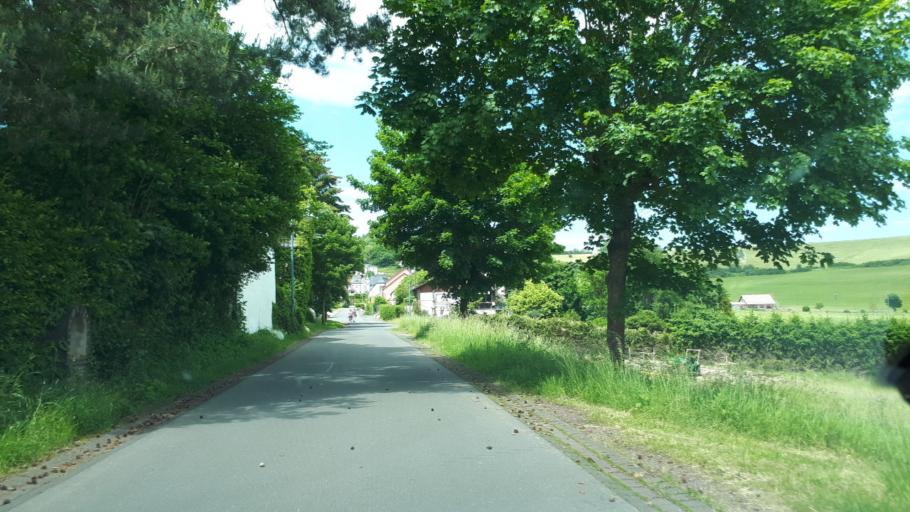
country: DE
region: Rheinland-Pfalz
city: Immerath
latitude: 50.1288
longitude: 6.9604
